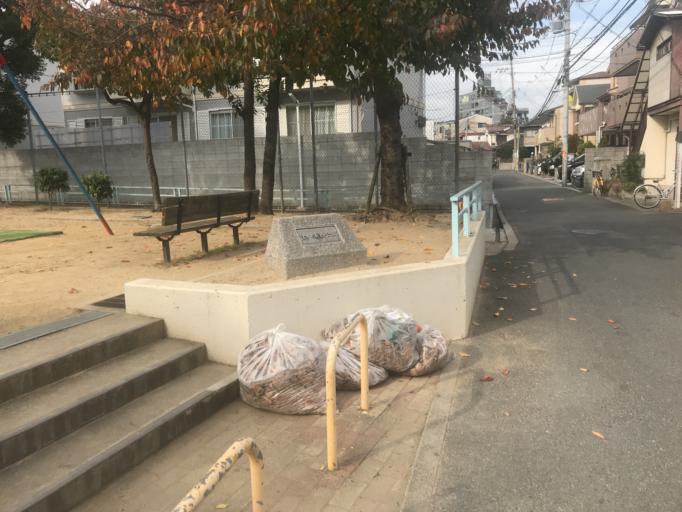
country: JP
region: Osaka
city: Suita
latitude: 34.7450
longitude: 135.4906
